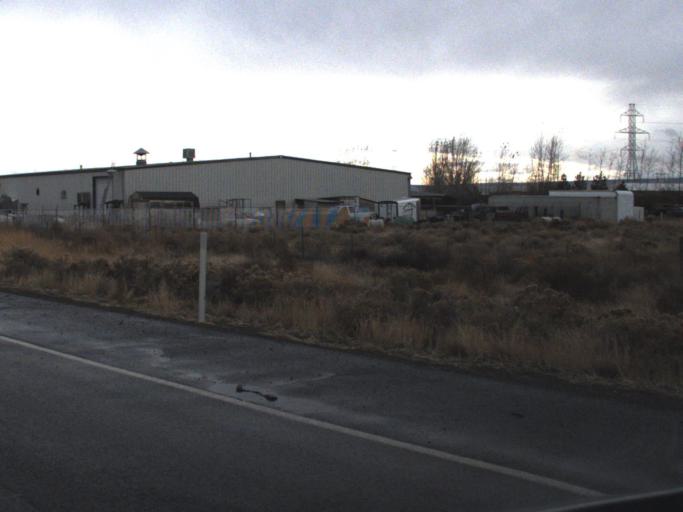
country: US
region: Washington
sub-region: Walla Walla County
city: Burbank
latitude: 46.2250
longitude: -119.0362
